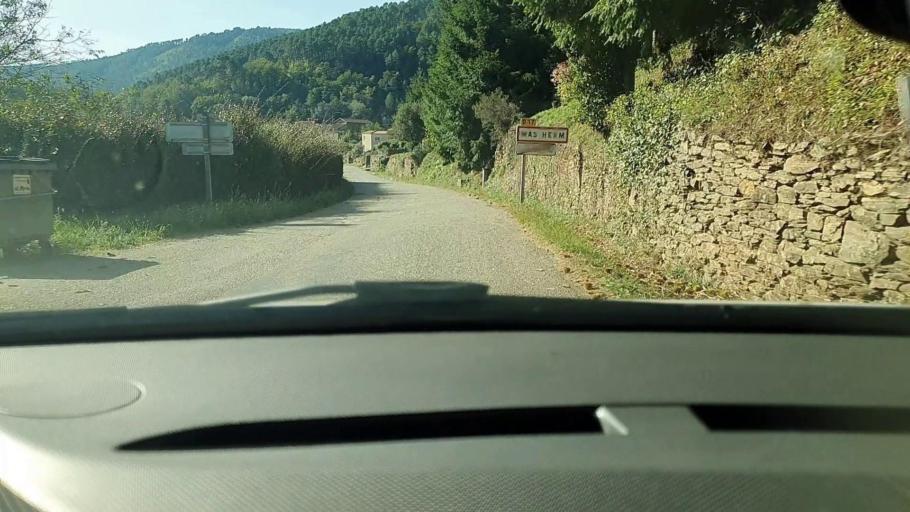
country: FR
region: Languedoc-Roussillon
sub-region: Departement du Gard
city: Besseges
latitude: 44.3063
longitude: 4.0594
